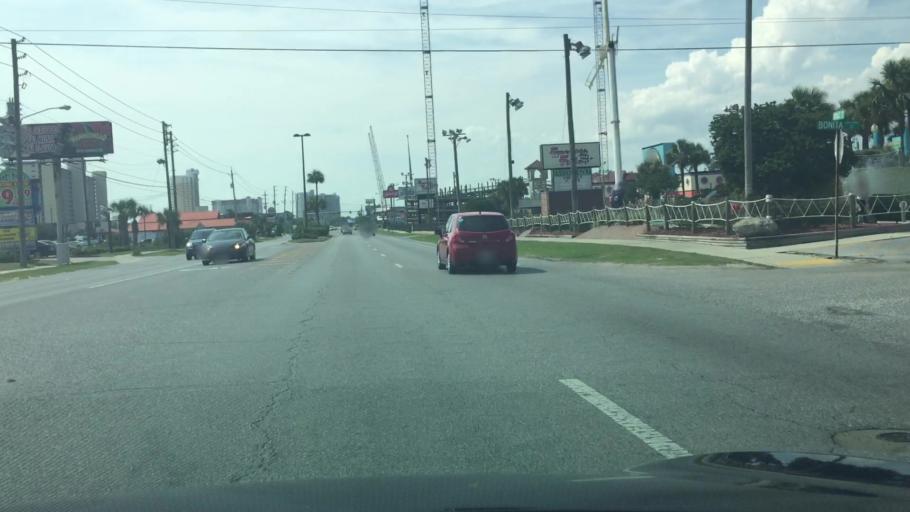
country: US
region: Florida
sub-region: Bay County
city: Panama City Beach
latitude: 30.1664
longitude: -85.7870
